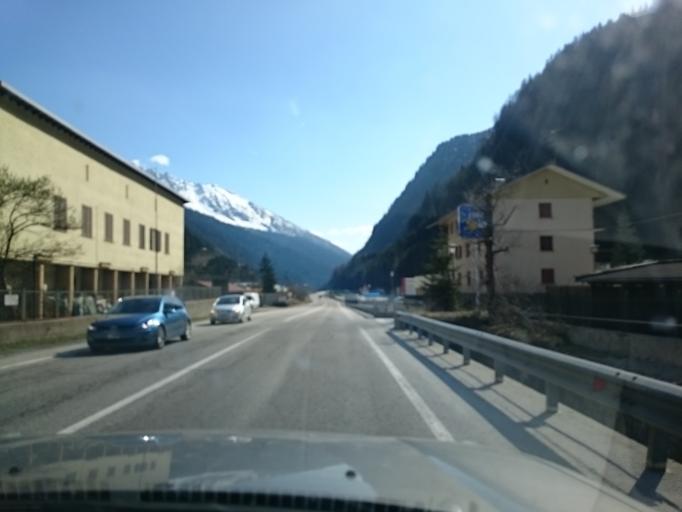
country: AT
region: Tyrol
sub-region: Politischer Bezirk Innsbruck Land
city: Gries am Brenner
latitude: 47.0010
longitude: 11.5037
